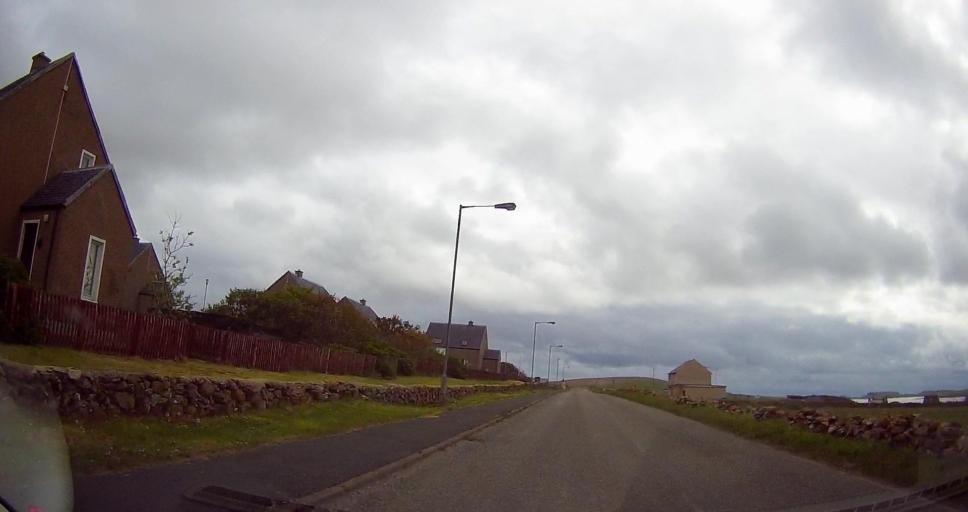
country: GB
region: Scotland
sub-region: Shetland Islands
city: Shetland
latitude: 60.7626
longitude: -0.8621
